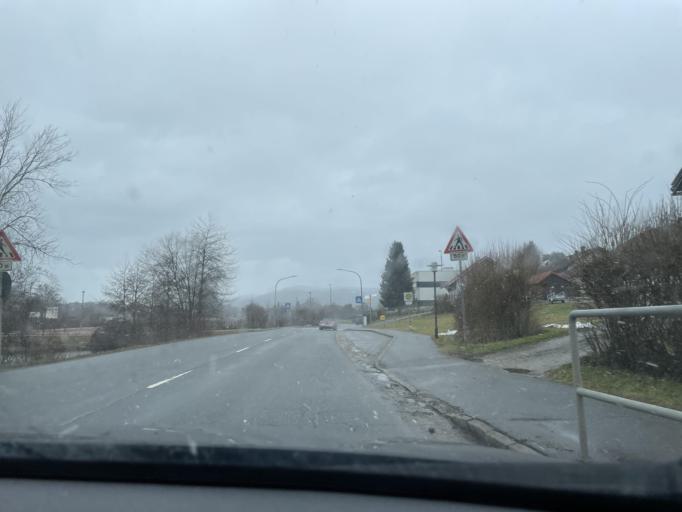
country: DE
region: Bavaria
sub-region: Upper Palatinate
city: Kotzting
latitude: 49.1800
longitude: 12.8575
